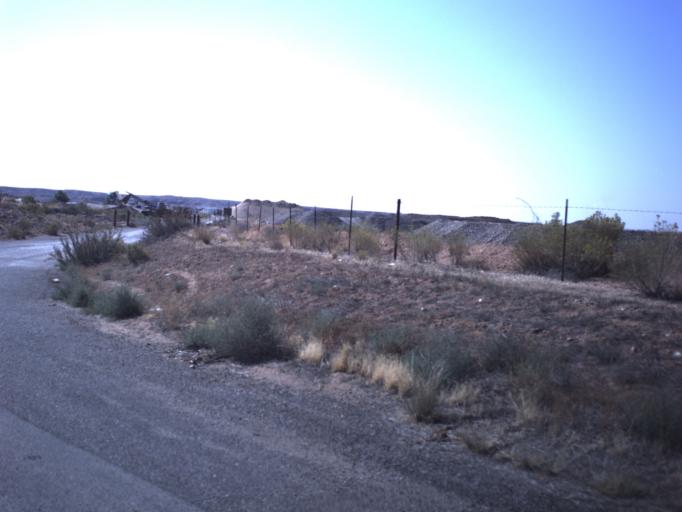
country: US
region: Utah
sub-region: San Juan County
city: Blanding
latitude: 37.2635
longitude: -109.6250
